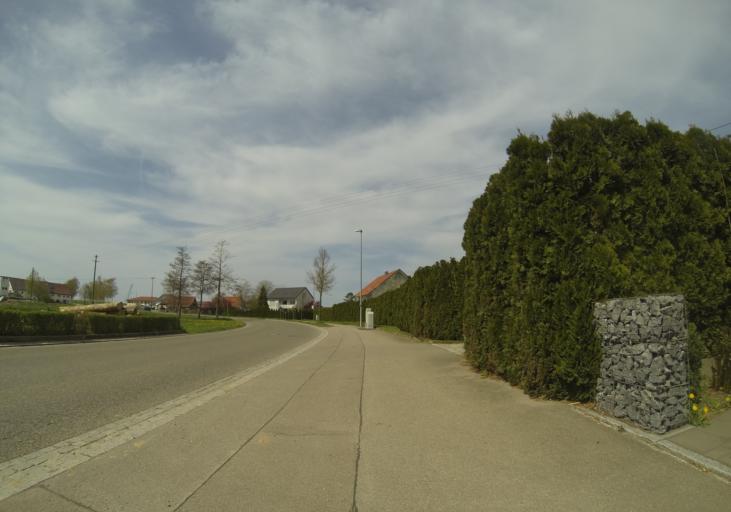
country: DE
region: Baden-Wuerttemberg
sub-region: Tuebingen Region
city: Huttisheim
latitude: 48.2607
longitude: 9.9548
